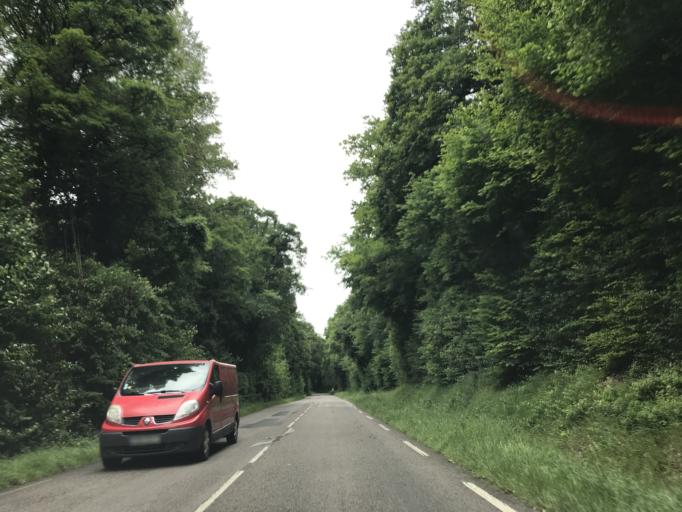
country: FR
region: Ile-de-France
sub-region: Departement des Yvelines
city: Rosny-sur-Seine
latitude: 48.9817
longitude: 1.6055
